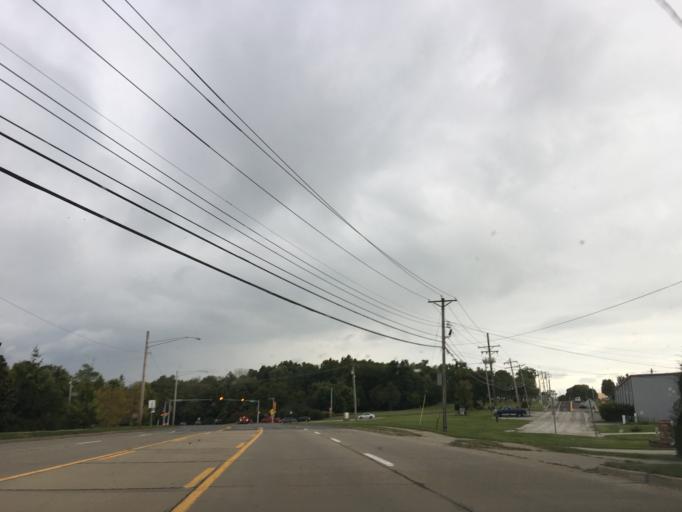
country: US
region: Missouri
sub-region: Saint Louis County
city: Maryland Heights
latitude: 38.7096
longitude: -90.4160
